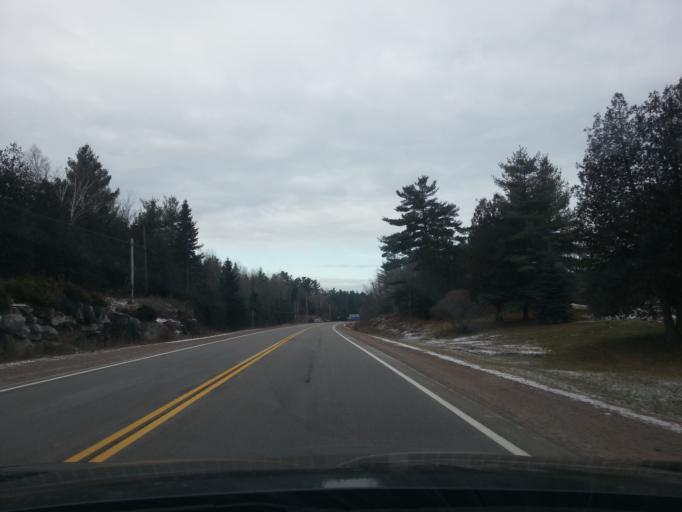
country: CA
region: Ontario
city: Deseronto
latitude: 44.5598
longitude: -77.2485
